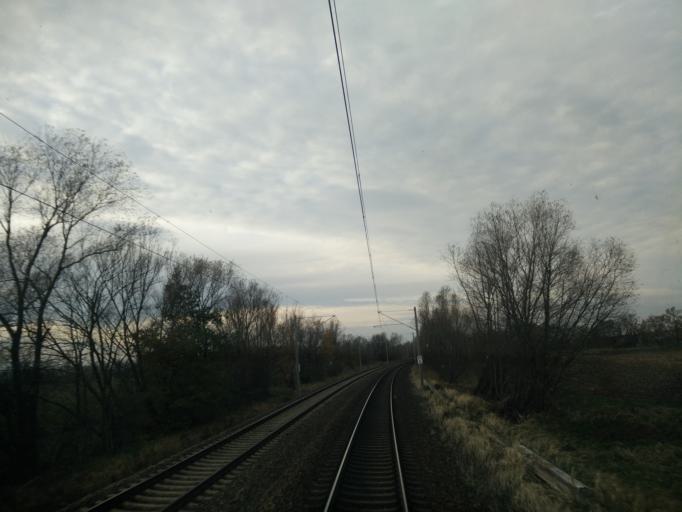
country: DE
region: Brandenburg
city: Luebben
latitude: 51.9580
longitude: 13.8291
